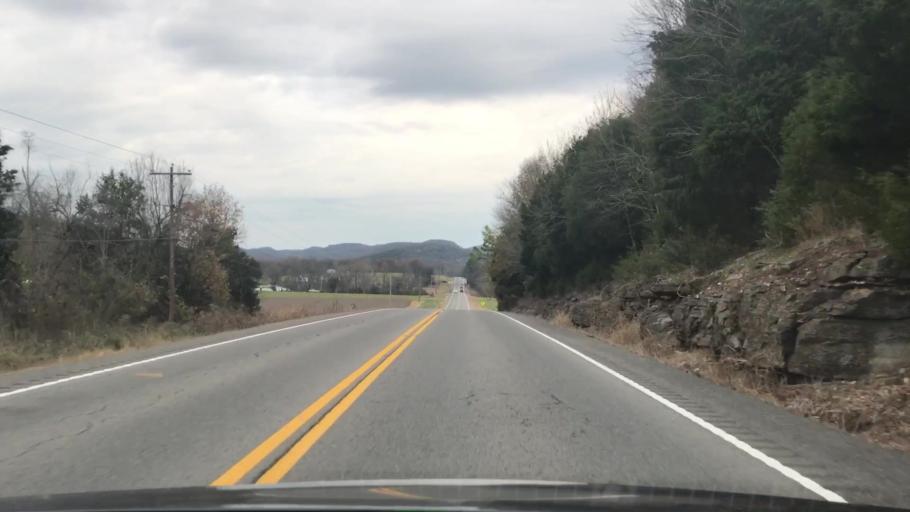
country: US
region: Tennessee
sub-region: Trousdale County
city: Hartsville
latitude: 36.4028
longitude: -86.1035
